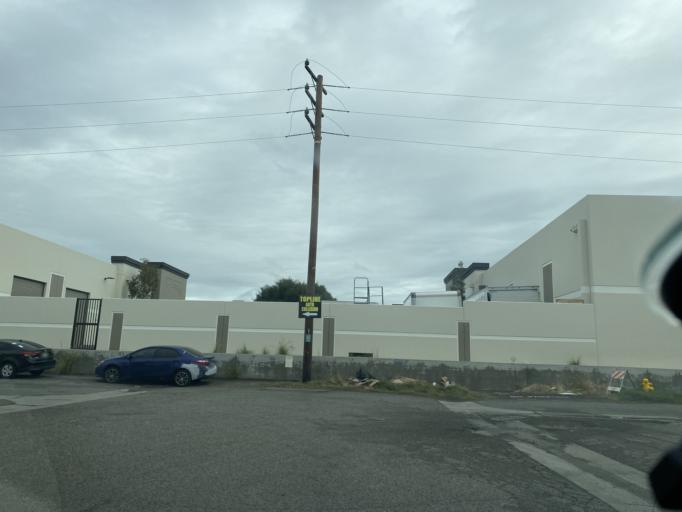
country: US
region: California
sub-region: Orange County
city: Fullerton
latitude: 33.8656
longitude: -117.9049
